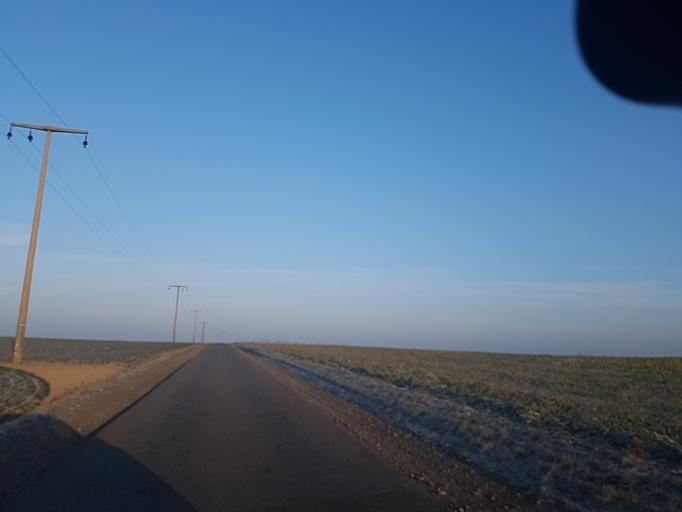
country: DE
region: Brandenburg
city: Niedergorsdorf
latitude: 51.9374
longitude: 13.0187
